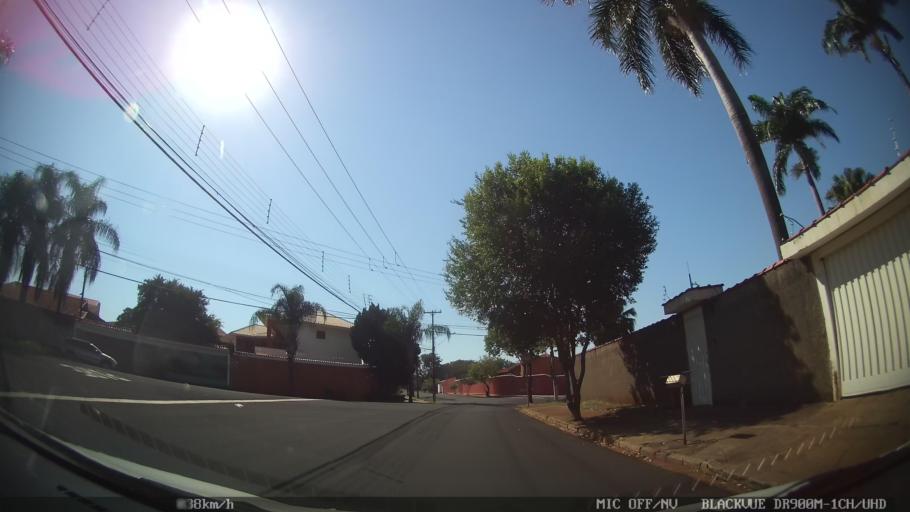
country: BR
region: Sao Paulo
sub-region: Ribeirao Preto
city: Ribeirao Preto
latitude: -21.2087
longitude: -47.7751
